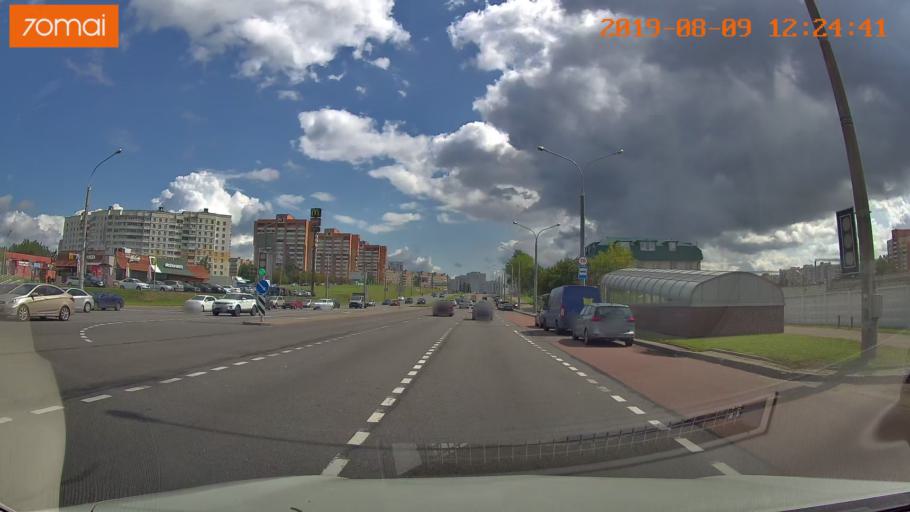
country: BY
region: Minsk
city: Novoye Medvezhino
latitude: 53.9297
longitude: 27.4883
